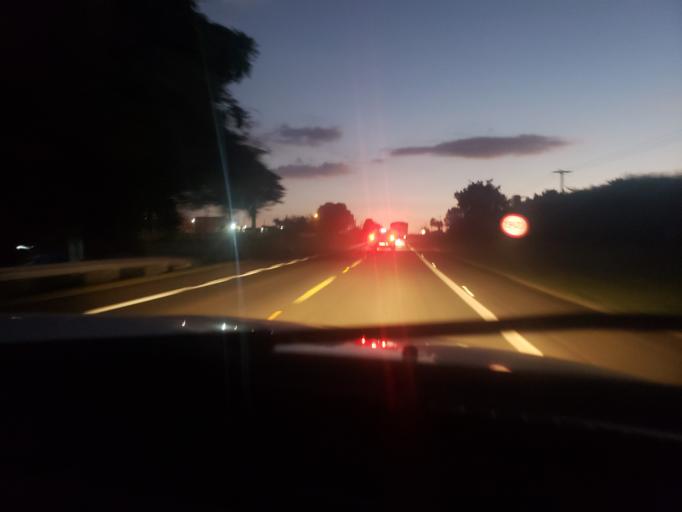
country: BR
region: Sao Paulo
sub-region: Conchal
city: Conchal
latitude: -22.3247
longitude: -47.1446
